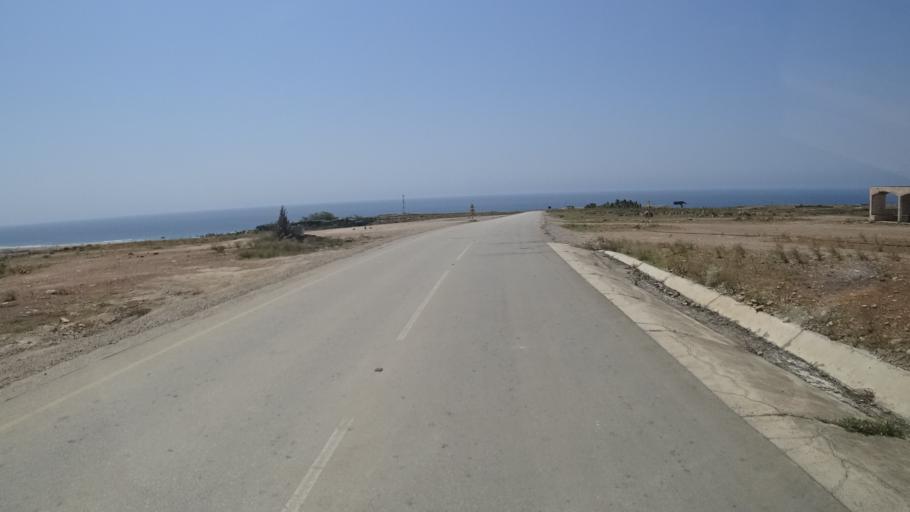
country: OM
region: Zufar
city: Salalah
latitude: 17.0398
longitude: 54.6130
